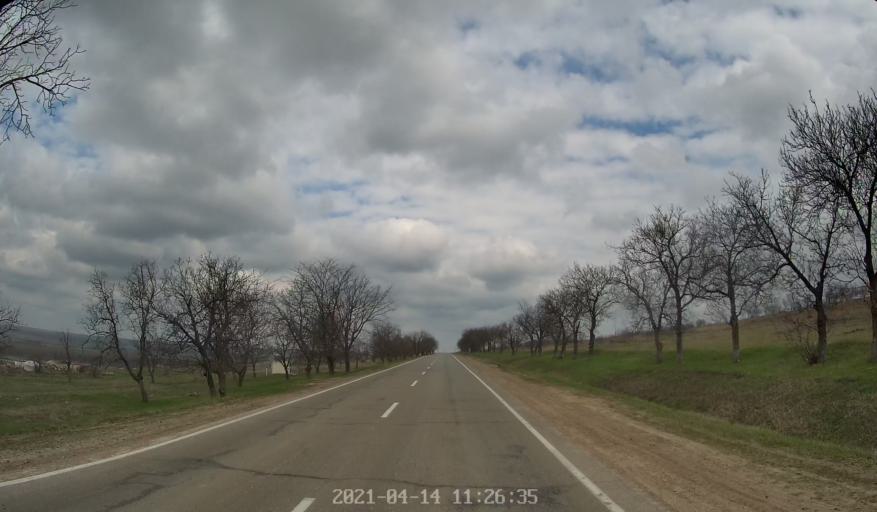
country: MD
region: Criuleni
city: Criuleni
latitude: 47.1653
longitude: 29.1633
